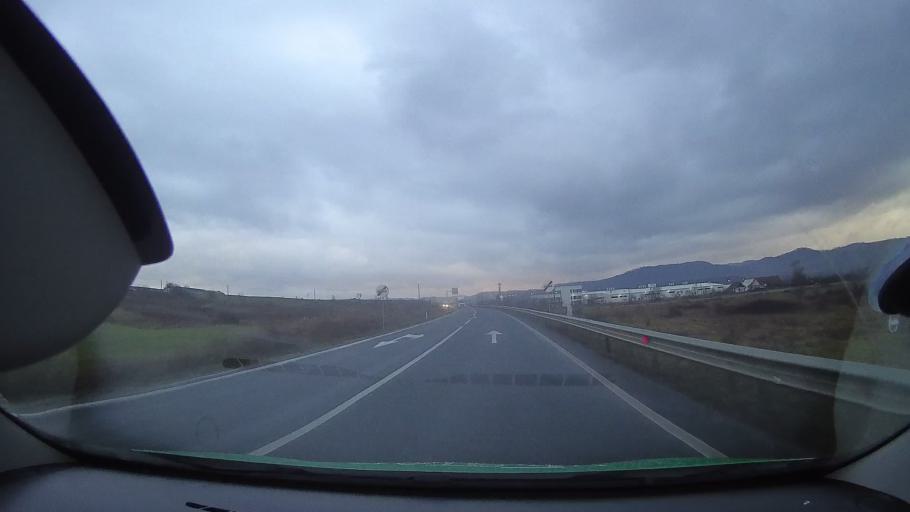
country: RO
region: Hunedoara
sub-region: Comuna Ribita
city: Ribita
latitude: 46.1629
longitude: 22.7563
